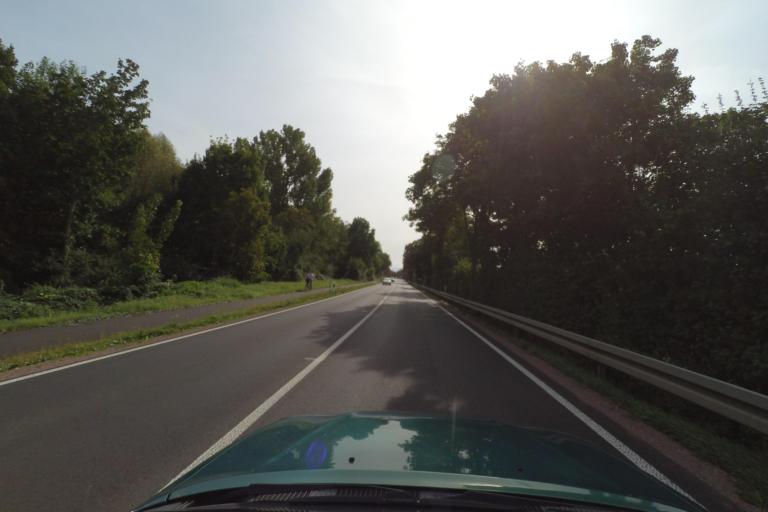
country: DE
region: Baden-Wuerttemberg
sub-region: Freiburg Region
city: Kenzingen
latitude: 48.1773
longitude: 7.7643
